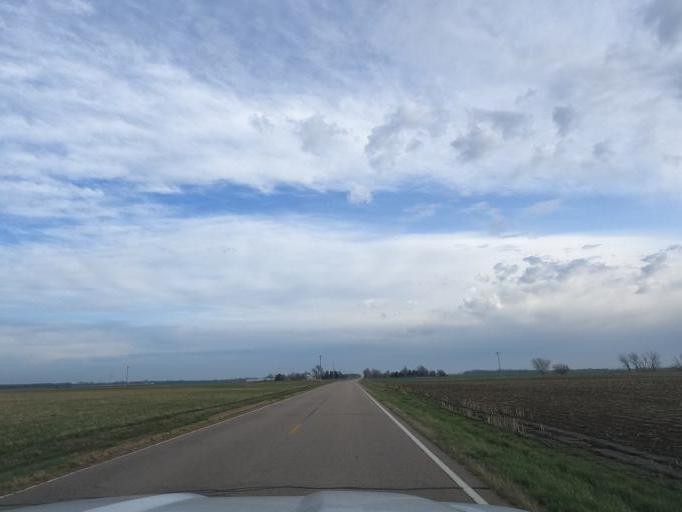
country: US
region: Kansas
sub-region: Reno County
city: Nickerson
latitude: 37.9978
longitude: -98.1788
